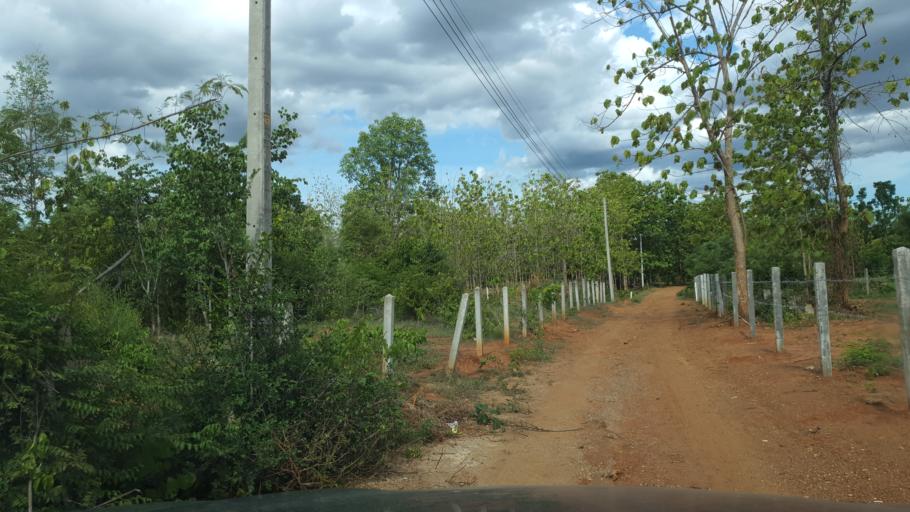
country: TH
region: Sukhothai
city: Thung Saliam
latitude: 17.3263
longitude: 99.5454
